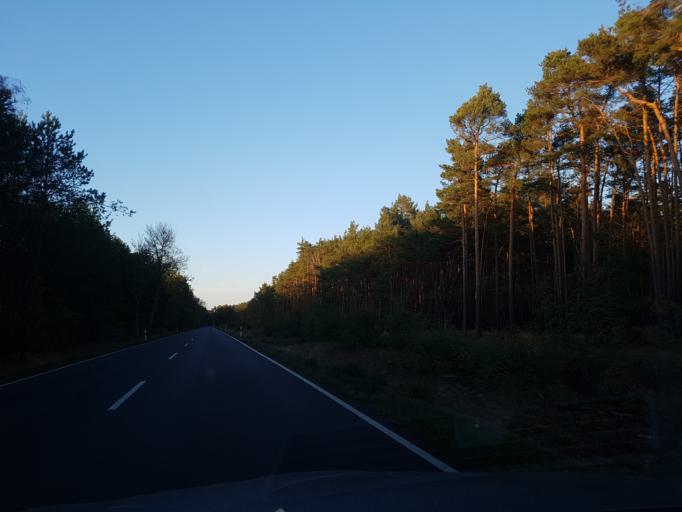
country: DE
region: Brandenburg
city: Schilda
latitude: 51.5817
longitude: 13.3575
